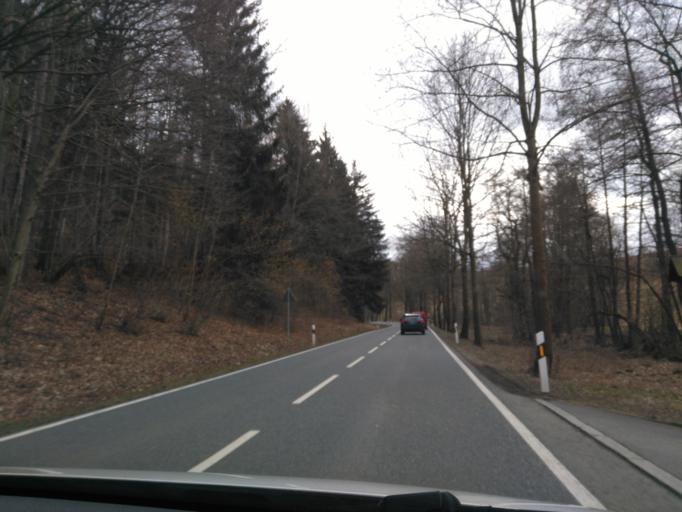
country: DE
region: Saxony
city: Wolkenstein
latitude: 50.6618
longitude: 13.0748
